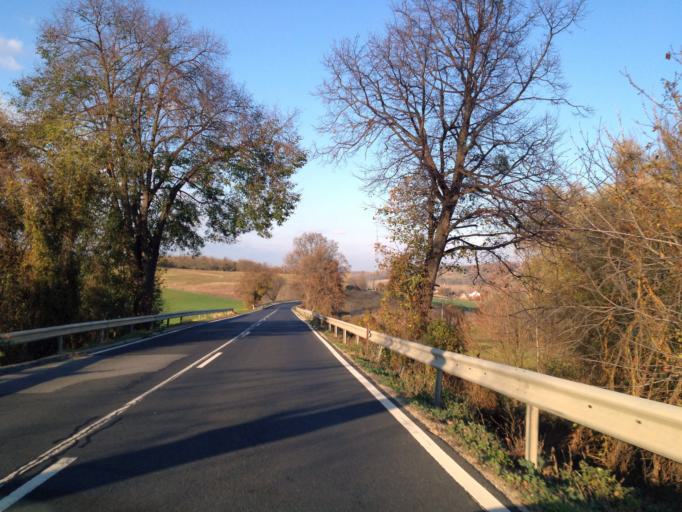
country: HU
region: Gyor-Moson-Sopron
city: Bakonyszentlaszlo
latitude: 47.3582
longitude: 17.8729
